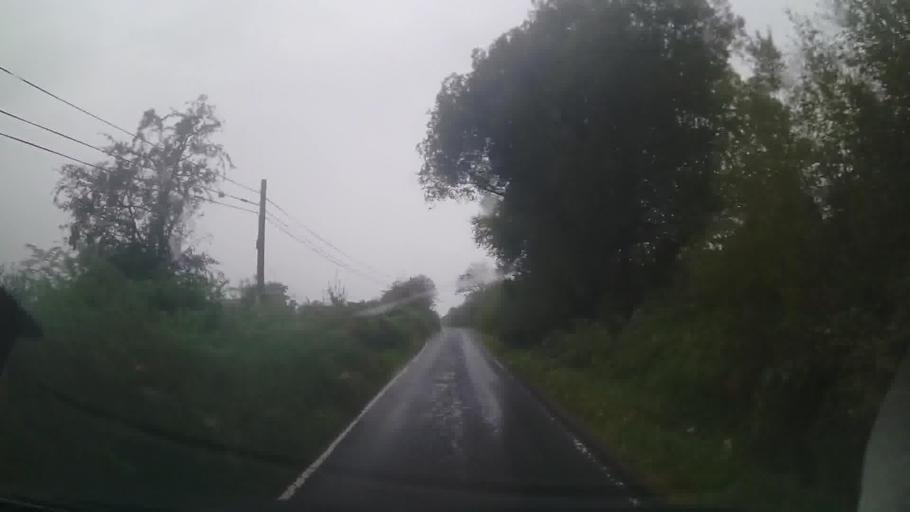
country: GB
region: Scotland
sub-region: Argyll and Bute
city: Isle Of Mull
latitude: 56.6902
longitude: -5.6029
